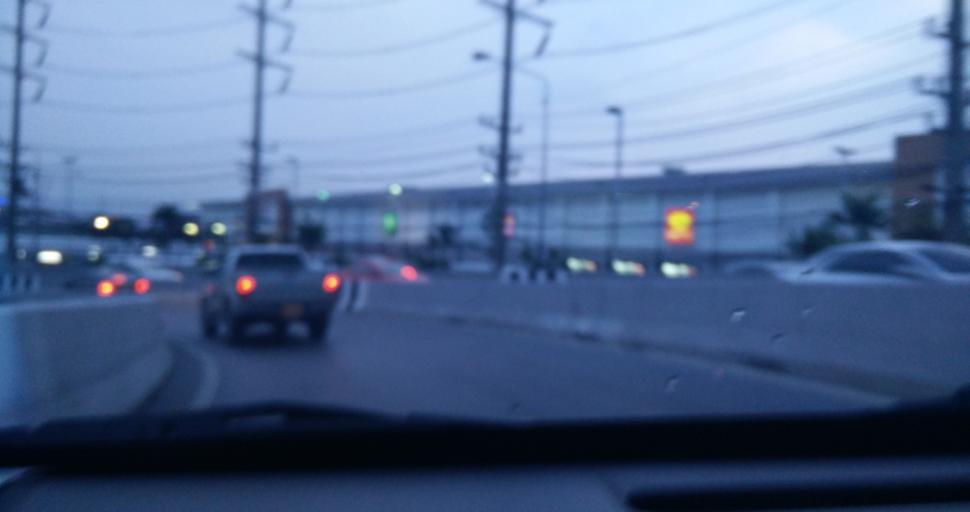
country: TH
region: Phra Nakhon Si Ayutthaya
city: Ban Bang Kadi Pathum Thani
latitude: 13.9948
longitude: 100.6138
